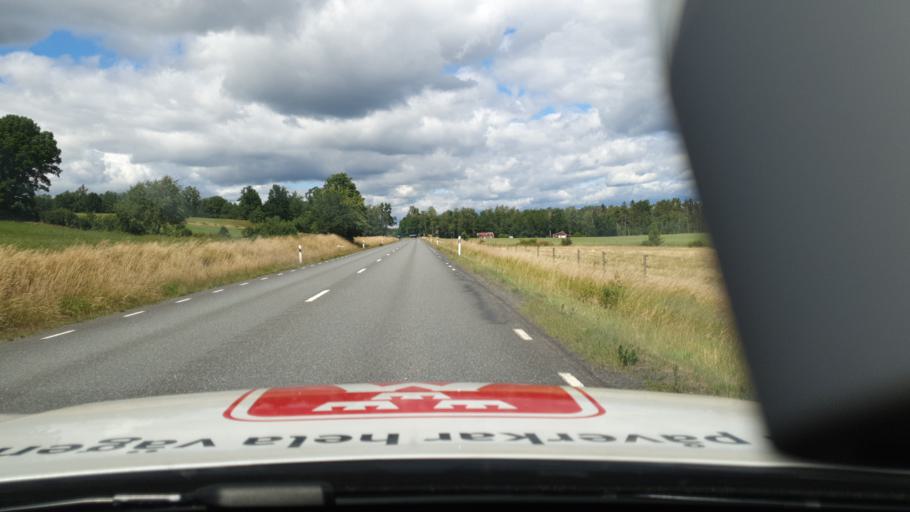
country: SE
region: Vaestra Goetaland
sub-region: Hjo Kommun
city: Hjo
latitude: 58.1309
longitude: 14.2195
